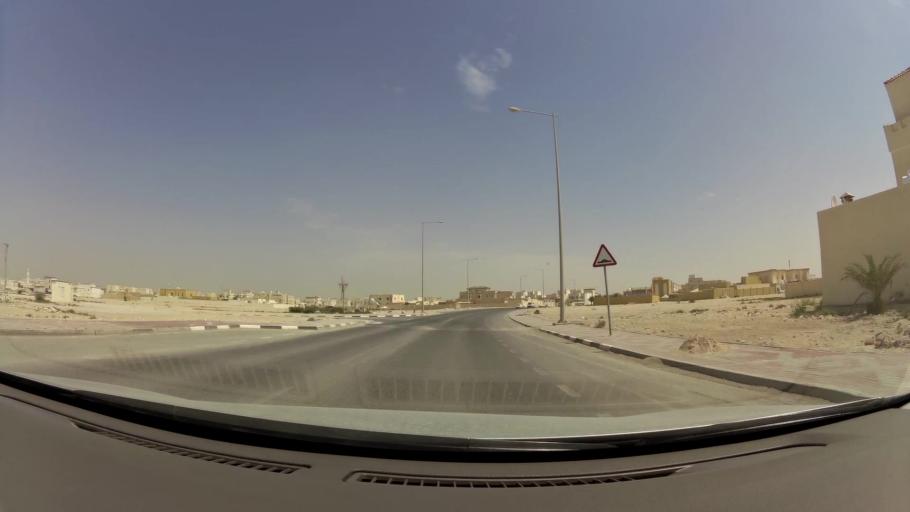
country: QA
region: Baladiyat ar Rayyan
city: Ar Rayyan
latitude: 25.2560
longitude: 51.4054
